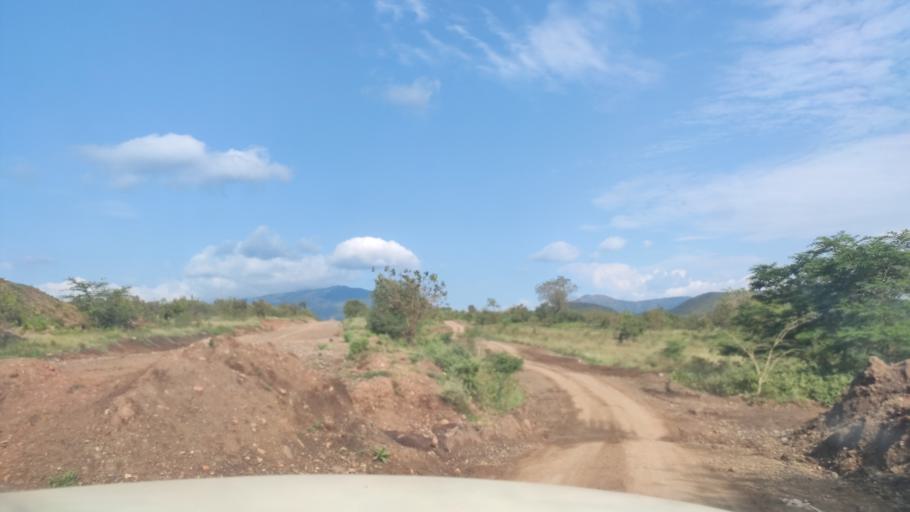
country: ET
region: Southern Nations, Nationalities, and People's Region
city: Felege Neway
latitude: 6.4345
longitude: 37.2713
